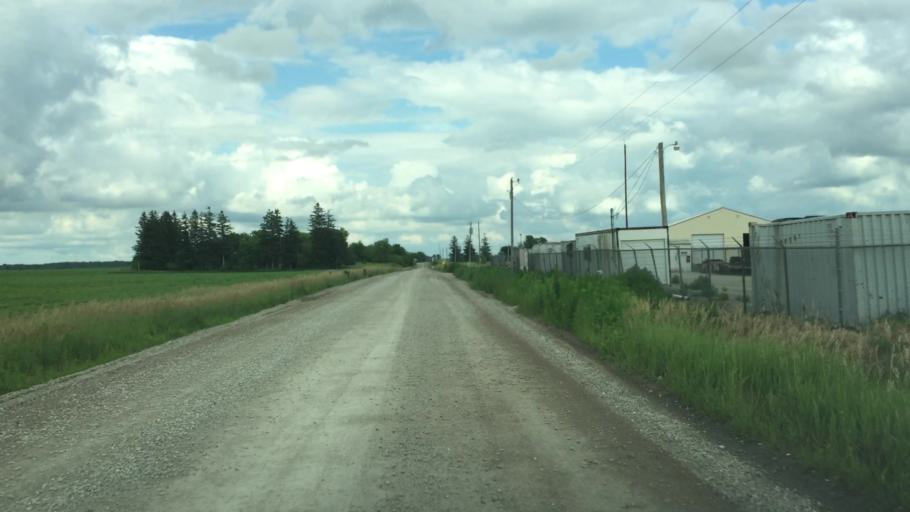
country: US
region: Iowa
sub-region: Jasper County
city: Newton
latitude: 41.7353
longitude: -93.0156
